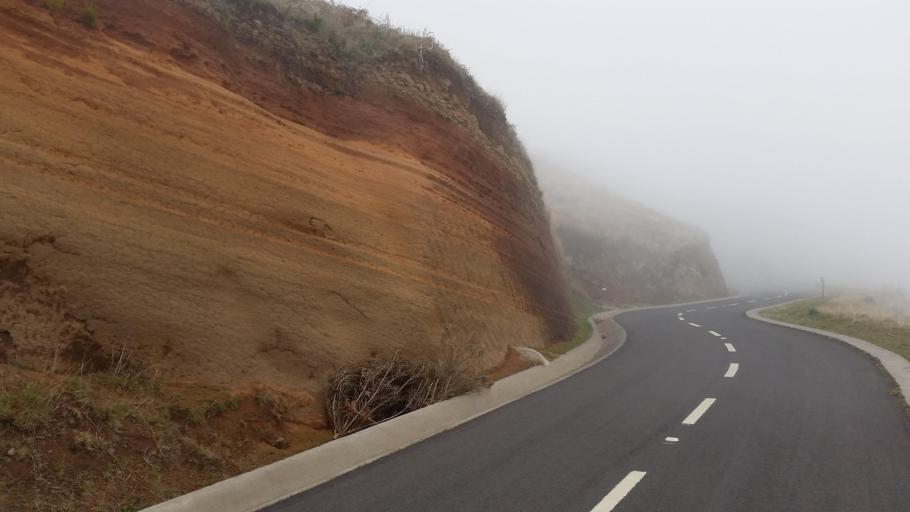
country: PT
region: Madeira
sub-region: Camara de Lobos
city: Curral das Freiras
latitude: 32.7234
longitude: -16.9255
